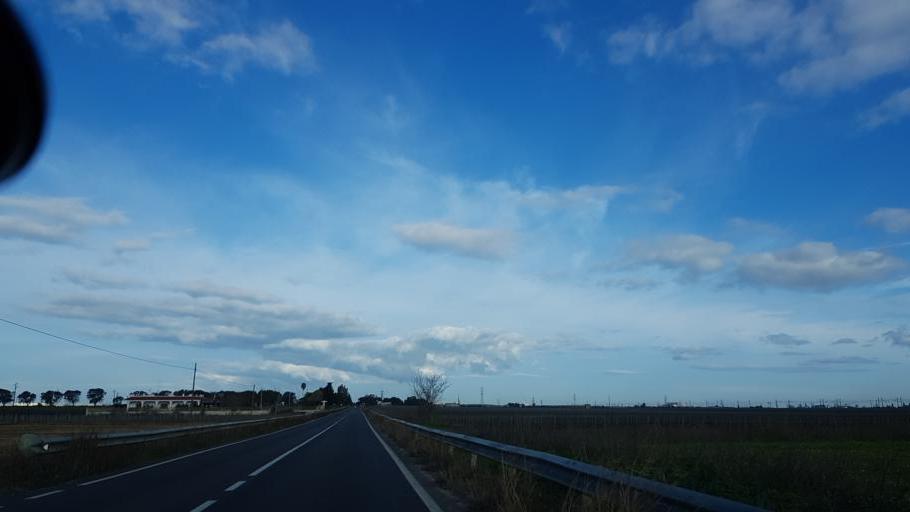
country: IT
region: Apulia
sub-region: Provincia di Brindisi
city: La Rosa
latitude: 40.5748
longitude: 17.9667
